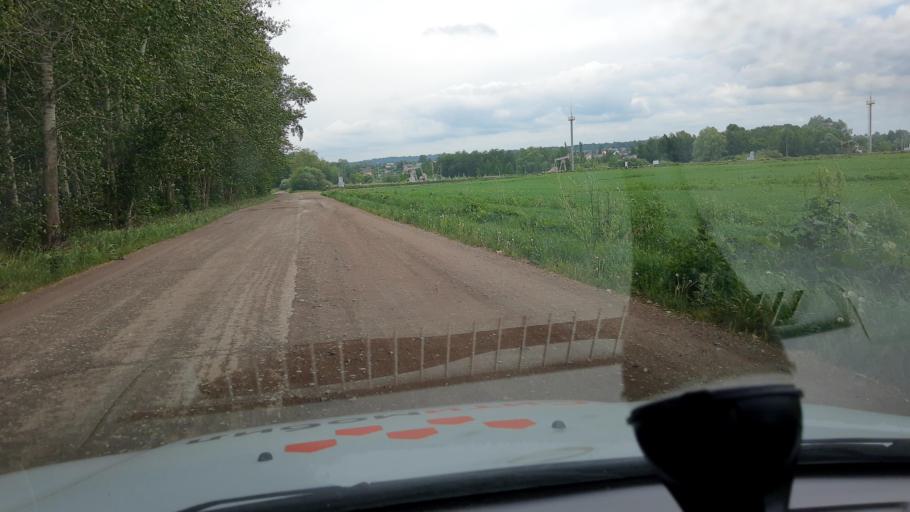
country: RU
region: Bashkortostan
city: Avdon
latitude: 54.6546
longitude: 55.6612
